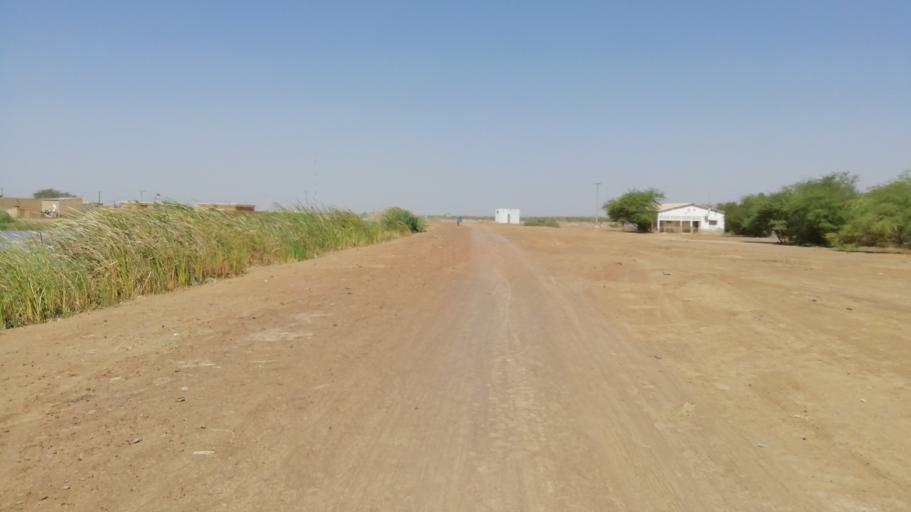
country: SN
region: Saint-Louis
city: Rosso
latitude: 16.3989
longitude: -16.0737
